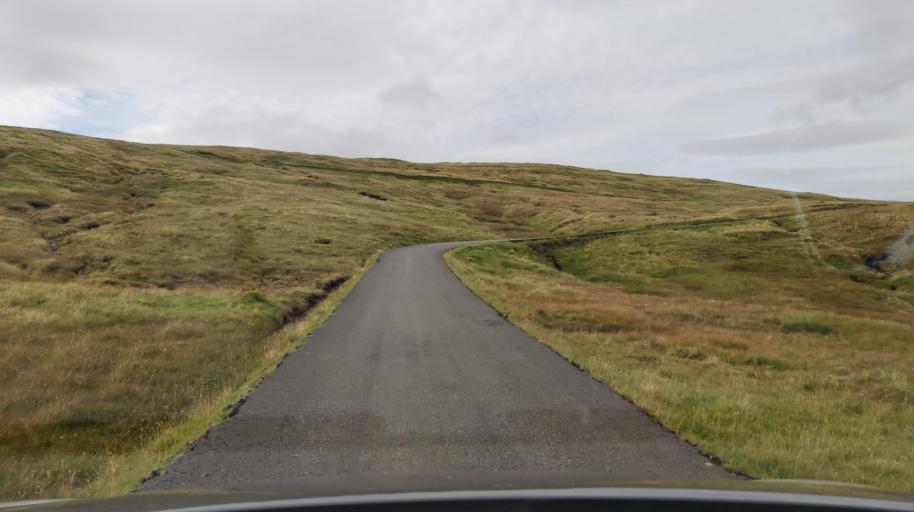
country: FO
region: Streymoy
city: Vestmanna
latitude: 62.1589
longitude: -7.1021
